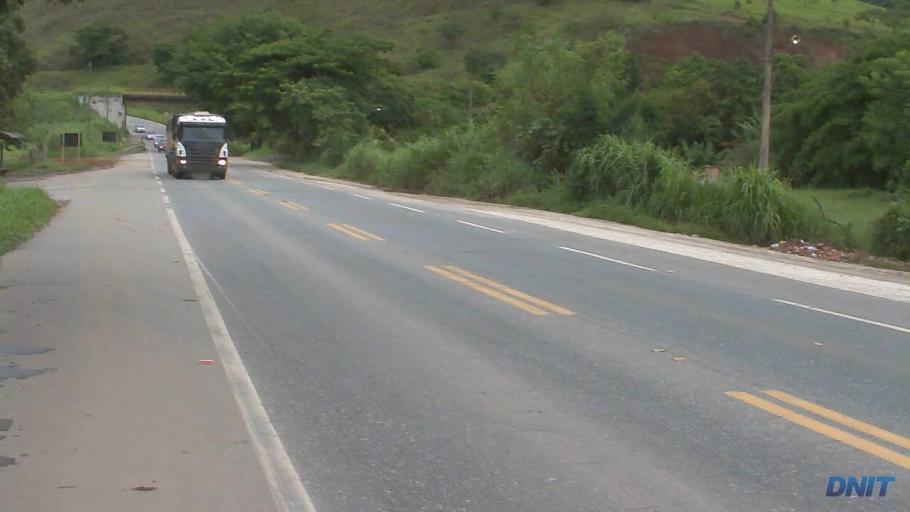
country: BR
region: Minas Gerais
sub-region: Nova Era
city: Nova Era
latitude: -19.7217
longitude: -43.0069
